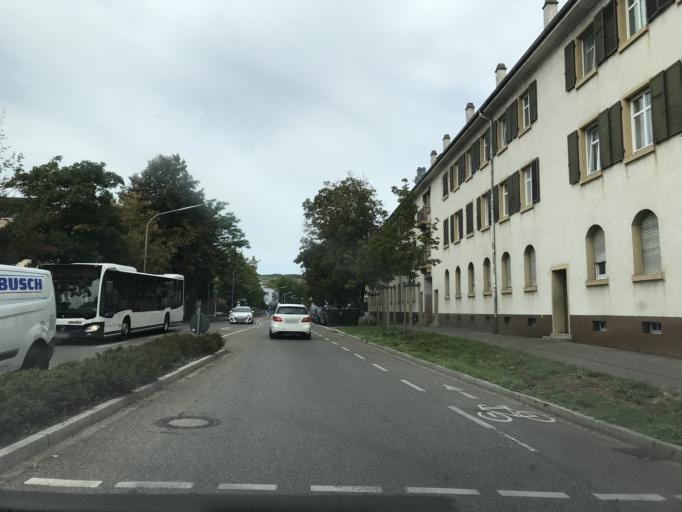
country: DE
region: Baden-Wuerttemberg
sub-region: Freiburg Region
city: Loerrach
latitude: 47.6177
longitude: 7.6665
